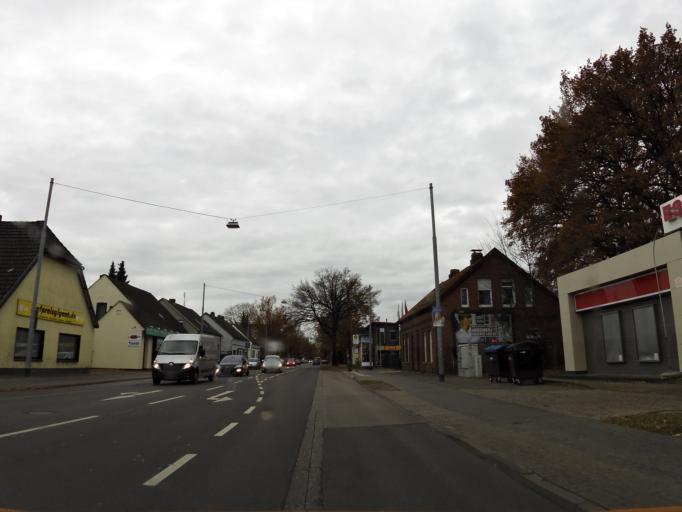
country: DE
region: Lower Saxony
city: Oldenburg
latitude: 53.1199
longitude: 8.2162
